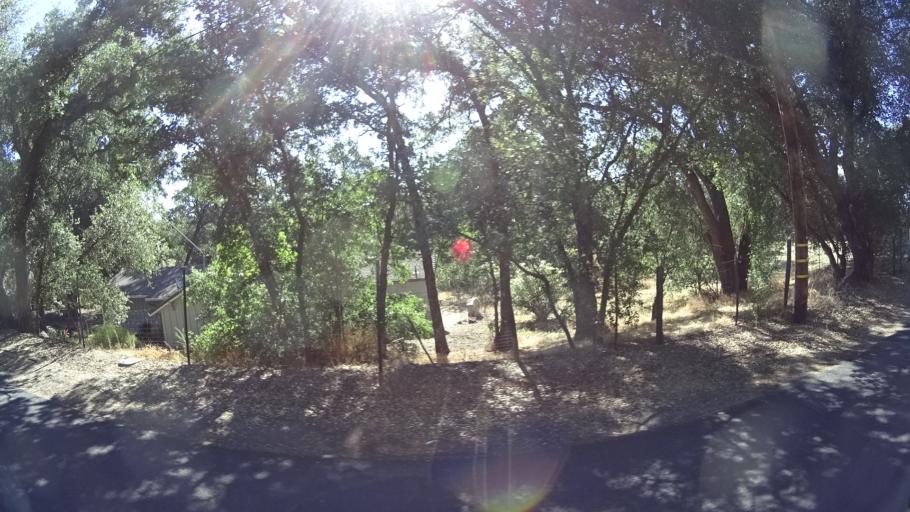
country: US
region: California
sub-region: Calaveras County
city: Murphys
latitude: 38.0896
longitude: -120.4727
